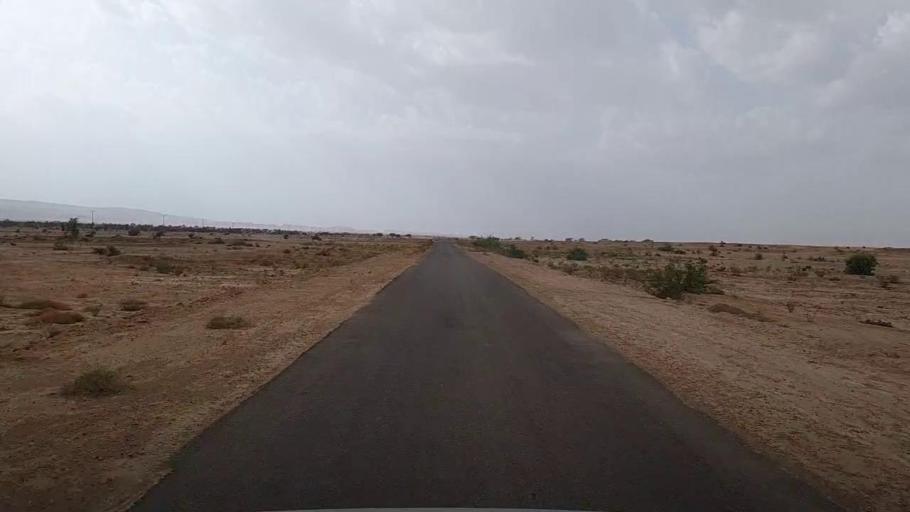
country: PK
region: Sindh
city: Jamshoro
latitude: 25.4357
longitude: 67.6856
